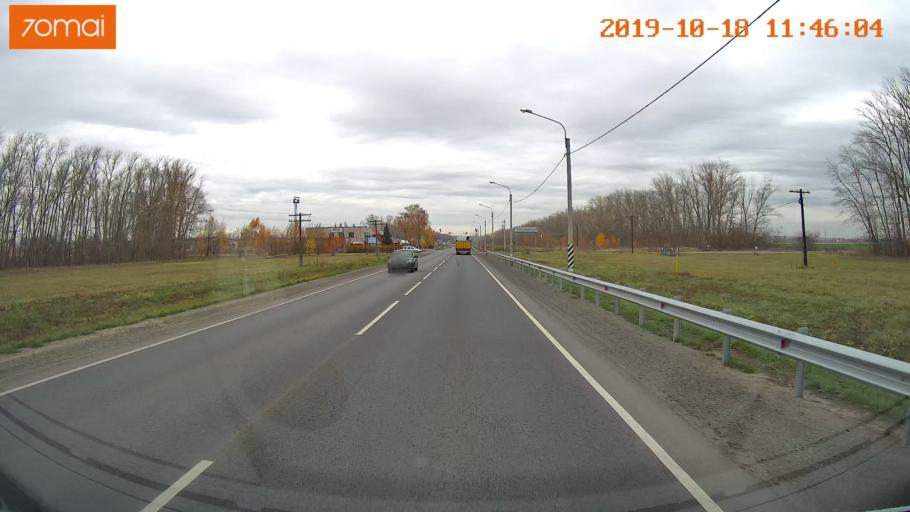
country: RU
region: Rjazan
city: Mikhaylov
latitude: 54.2163
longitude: 38.9787
